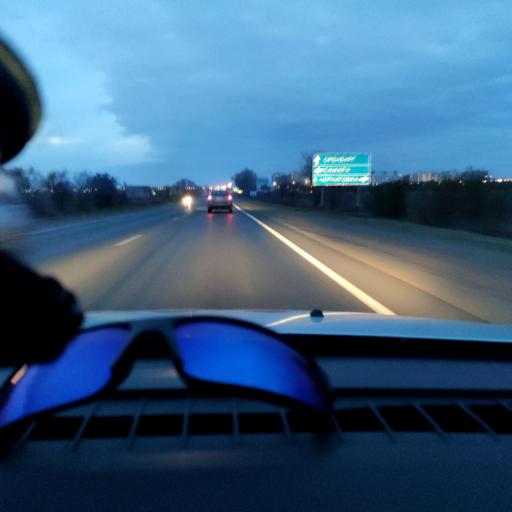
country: RU
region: Samara
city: Samara
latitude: 53.0878
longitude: 50.1455
